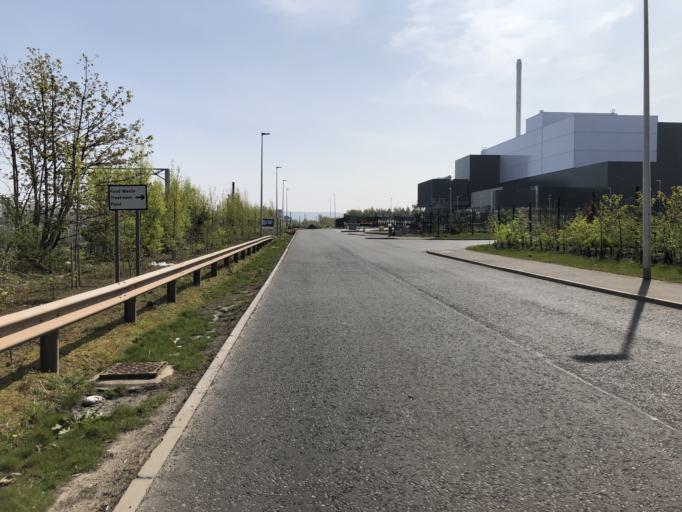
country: GB
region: Scotland
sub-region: Midlothian
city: Dalkeith
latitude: 55.9263
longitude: -3.0851
